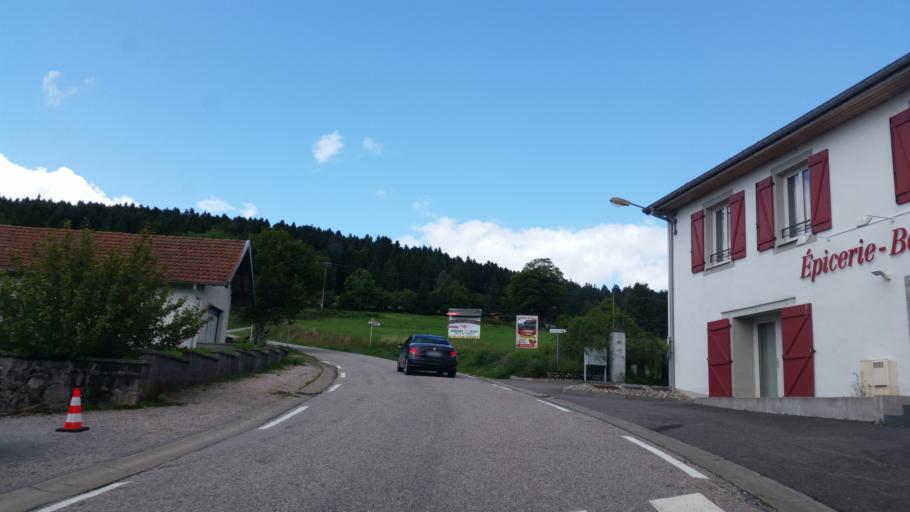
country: FR
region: Lorraine
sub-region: Departement des Vosges
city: Granges-sur-Vologne
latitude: 48.0945
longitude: 6.8051
